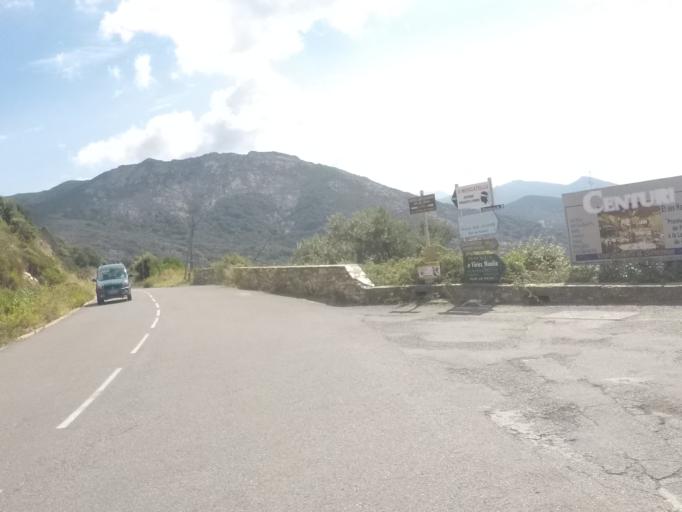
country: FR
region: Corsica
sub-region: Departement de la Haute-Corse
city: Brando
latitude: 42.9597
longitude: 9.3679
